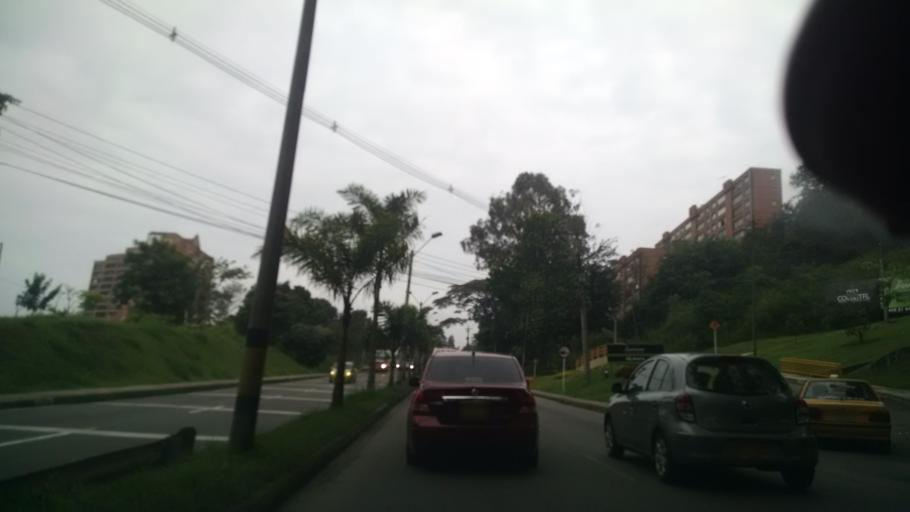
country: CO
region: Antioquia
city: Medellin
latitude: 6.2155
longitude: -75.5575
